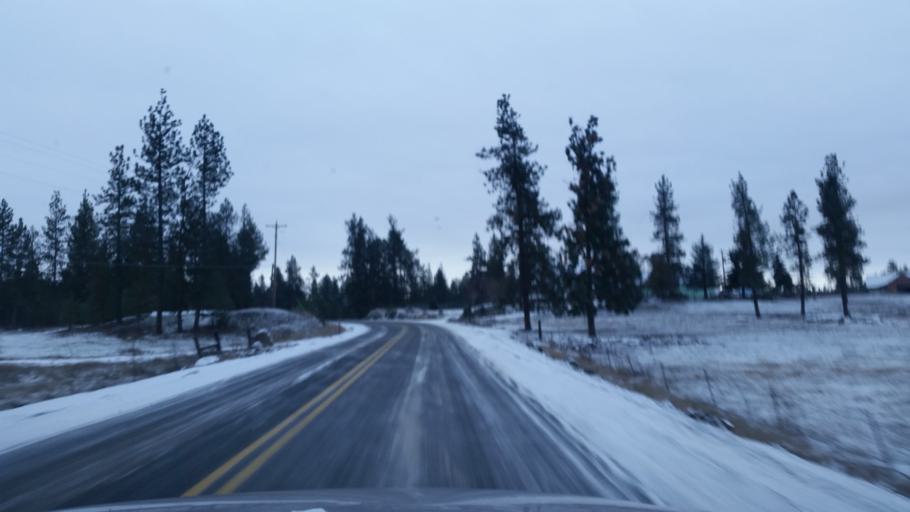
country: US
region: Washington
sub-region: Spokane County
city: Cheney
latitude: 47.4701
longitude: -117.5419
